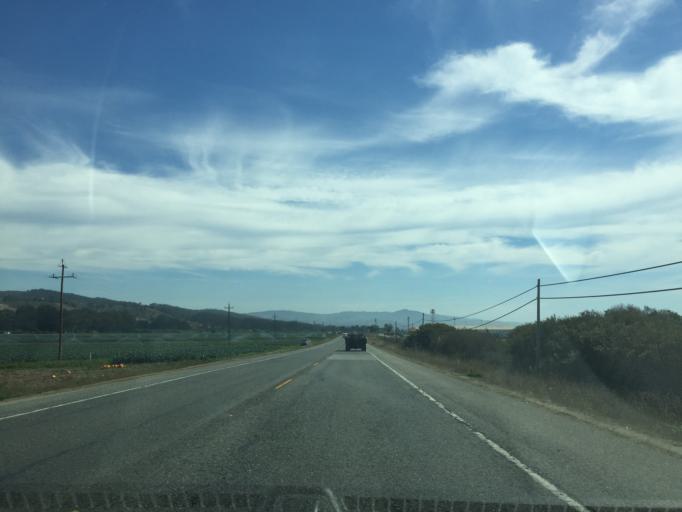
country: US
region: California
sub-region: San Mateo County
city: Moss Beach
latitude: 37.5184
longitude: -122.5017
